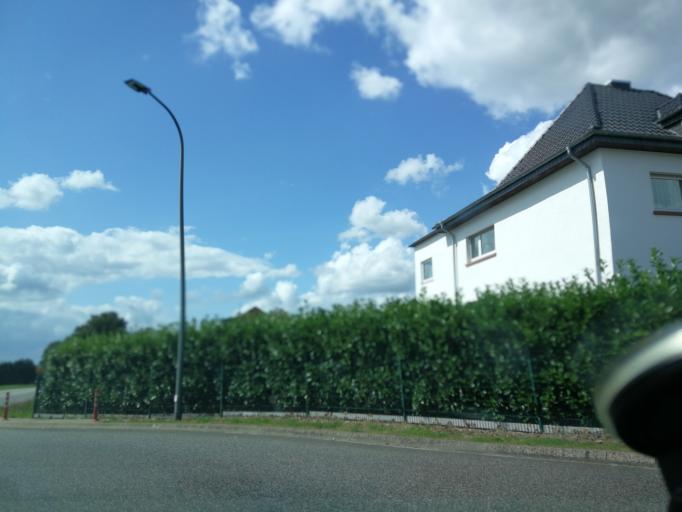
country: DE
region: Rheinland-Pfalz
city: Binsfeld
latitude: 49.9650
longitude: 6.7018
